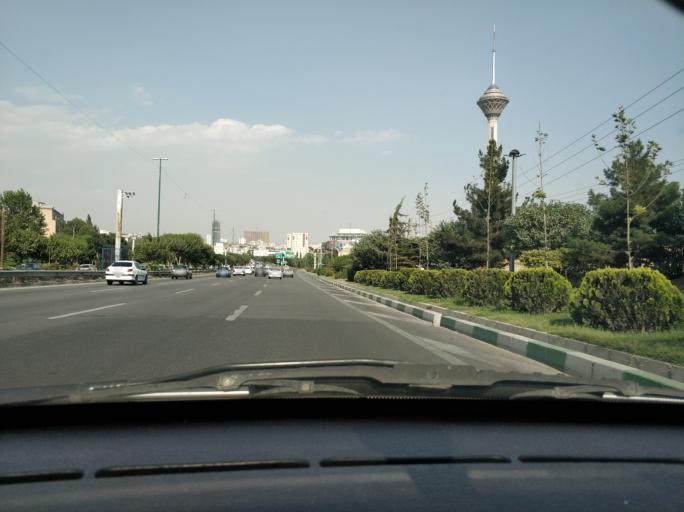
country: IR
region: Tehran
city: Tehran
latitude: 35.7492
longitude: 51.3643
